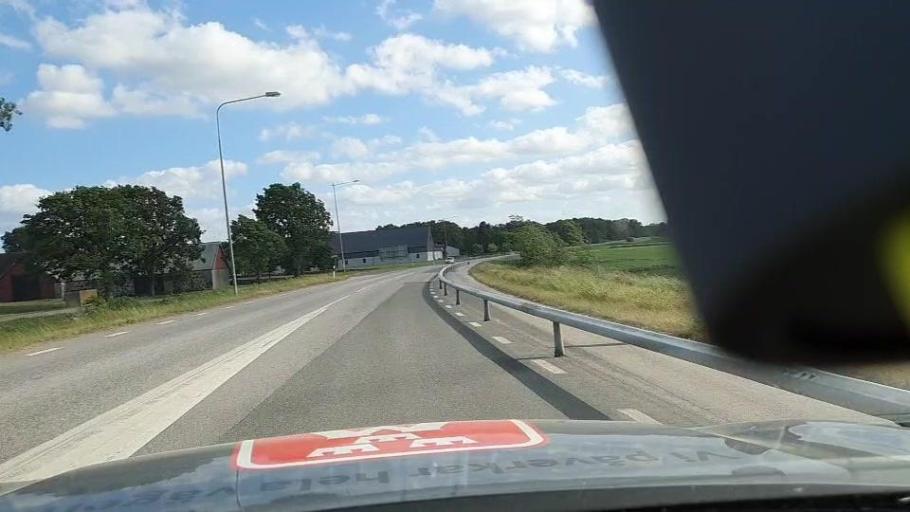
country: SE
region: Blekinge
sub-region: Karlshamns Kommun
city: Morrum
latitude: 56.1111
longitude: 14.6751
